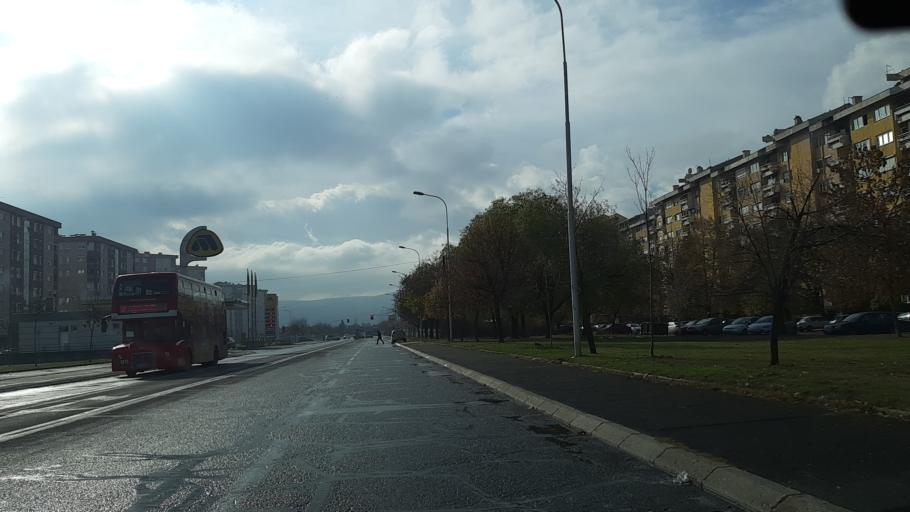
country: MK
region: Kisela Voda
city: Usje
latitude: 41.9851
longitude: 21.4834
